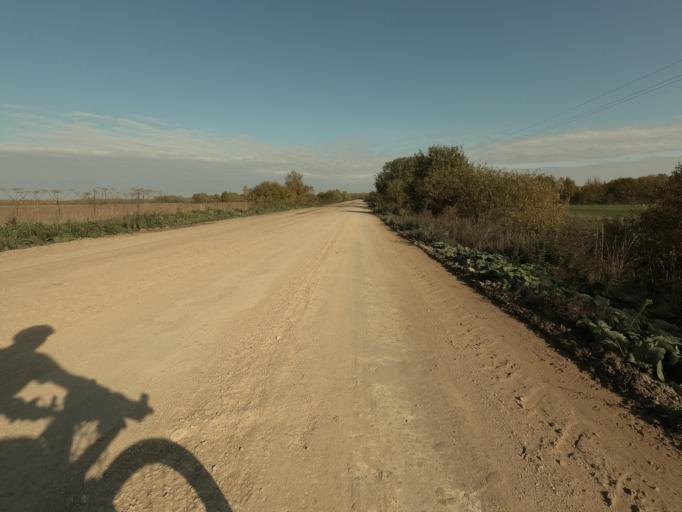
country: RU
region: Novgorod
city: Batetskiy
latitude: 58.8143
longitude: 30.6979
